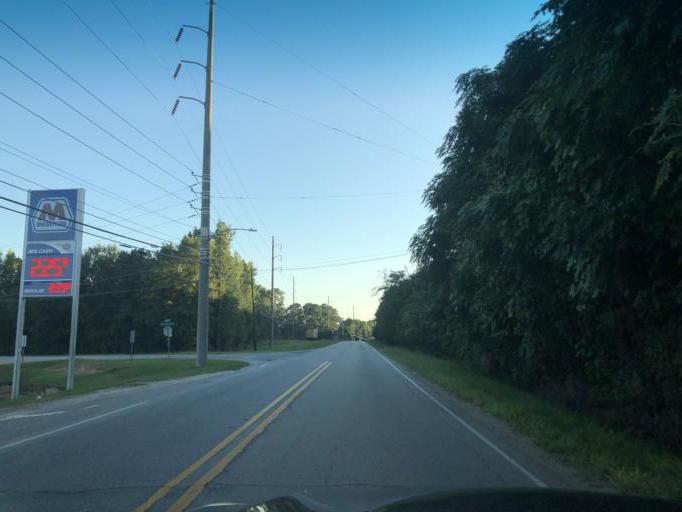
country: US
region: Georgia
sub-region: Muscogee County
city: Columbus
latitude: 32.5436
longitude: -84.8945
